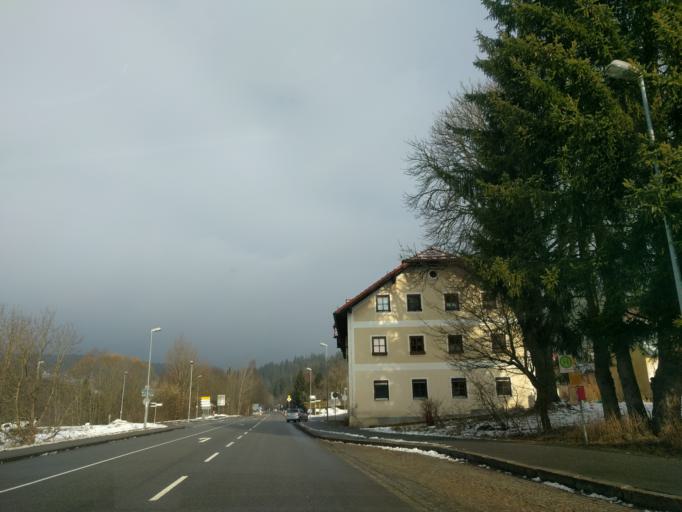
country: DE
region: Bavaria
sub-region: Lower Bavaria
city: Zwiesel
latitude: 49.0350
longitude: 13.2339
